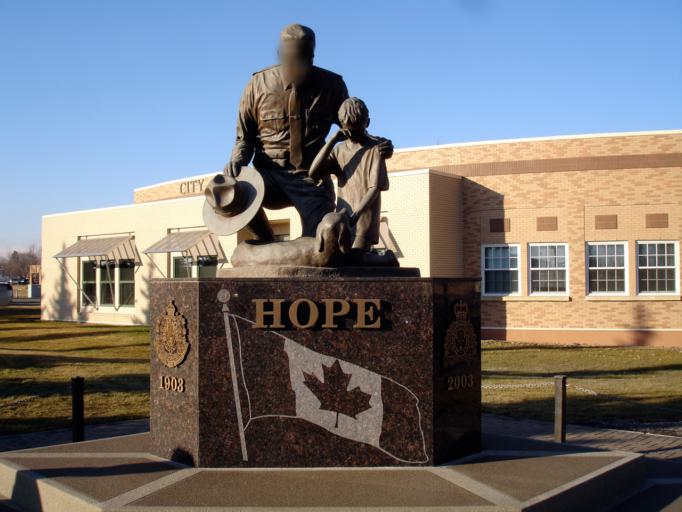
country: CA
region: Saskatchewan
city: Lloydminster
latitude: 53.2783
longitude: -110.0062
